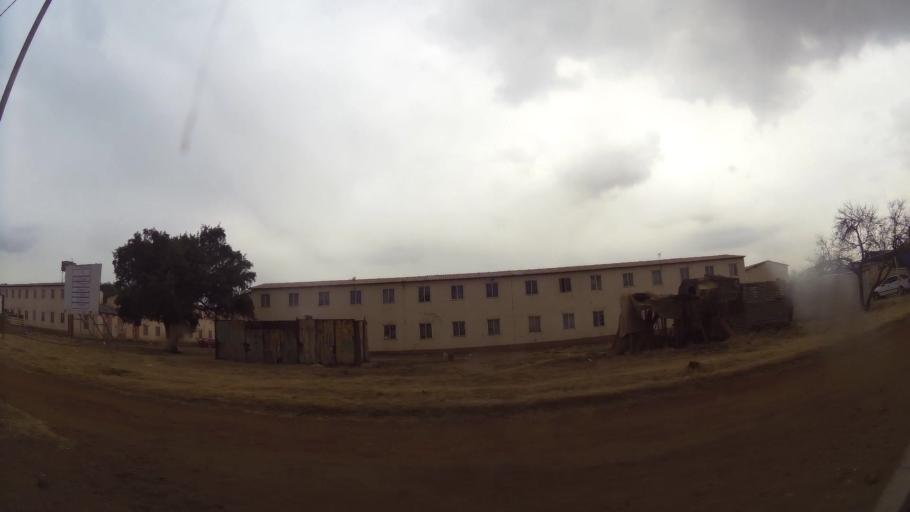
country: ZA
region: Gauteng
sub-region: Ekurhuleni Metropolitan Municipality
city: Germiston
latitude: -26.3630
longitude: 28.1437
